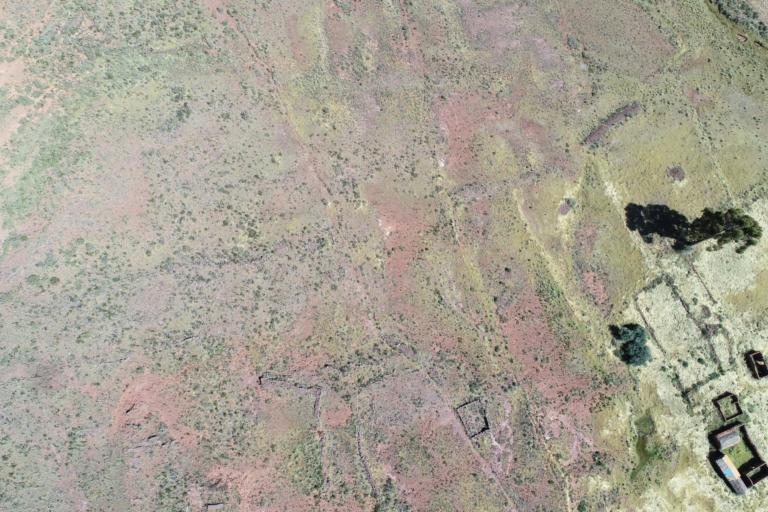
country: BO
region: La Paz
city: Tiahuanaco
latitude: -16.6082
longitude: -68.7728
